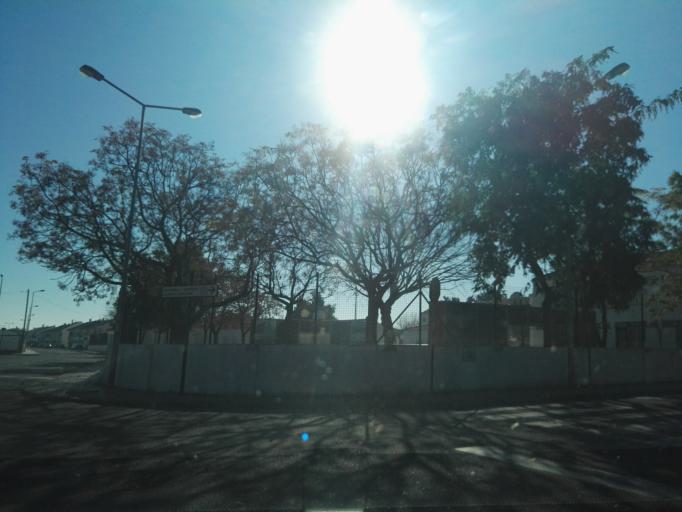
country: PT
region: Santarem
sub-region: Benavente
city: Samora Correia
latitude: 38.9351
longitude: -8.8692
